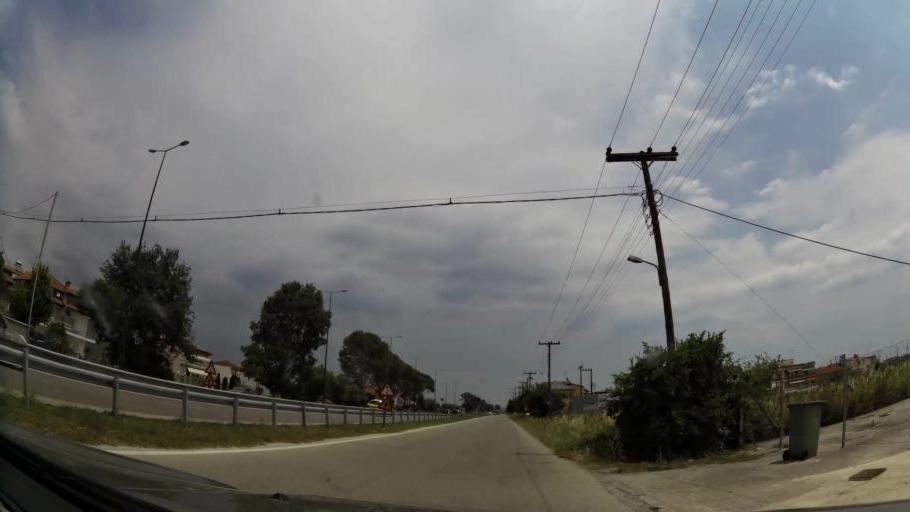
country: GR
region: Central Macedonia
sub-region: Nomos Pierias
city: Kallithea
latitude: 40.2697
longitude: 22.5781
